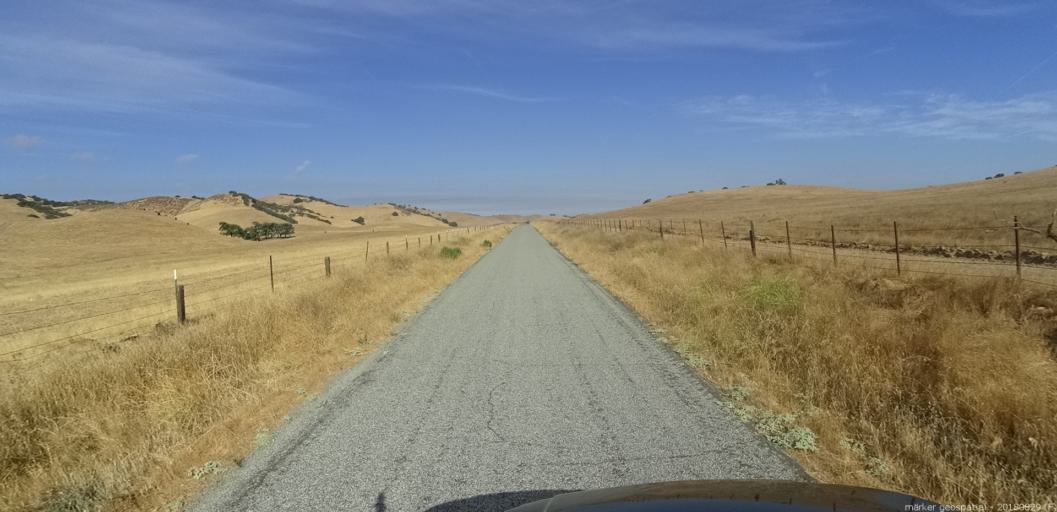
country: US
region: California
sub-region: Monterey County
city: King City
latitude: 36.0275
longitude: -120.9549
